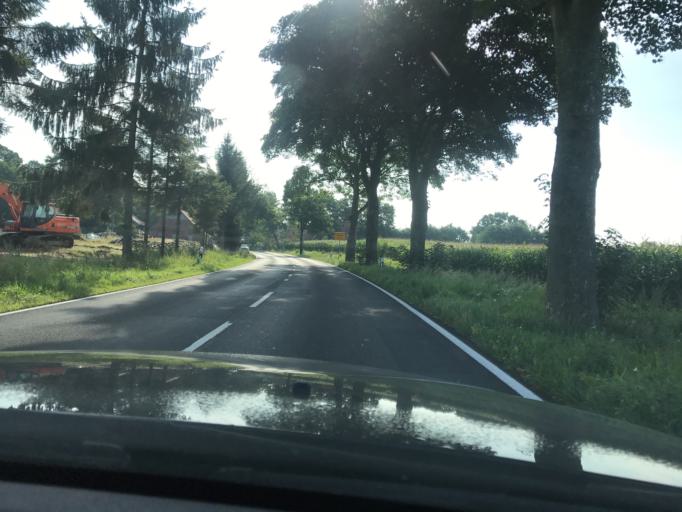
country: DE
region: Lower Saxony
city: Bawinkel
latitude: 52.6602
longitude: 7.4180
